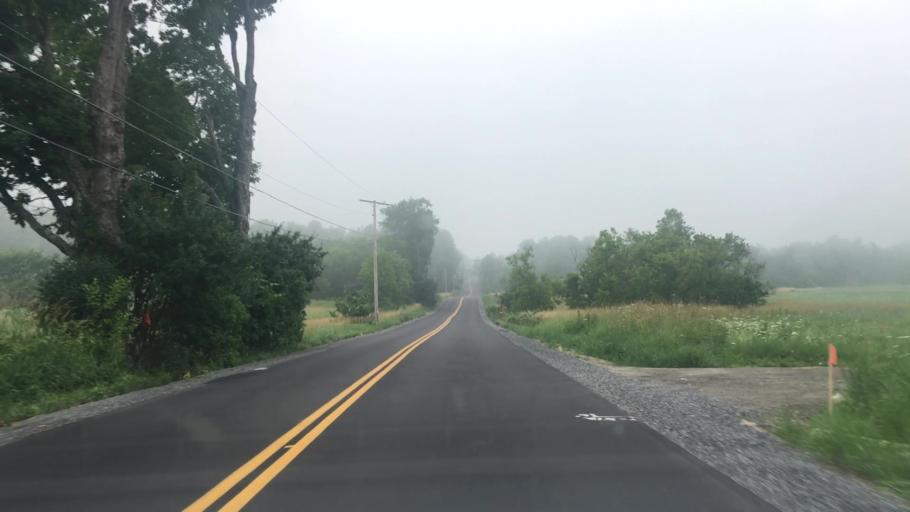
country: US
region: Maine
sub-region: Kennebec County
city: Oakland
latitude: 44.5117
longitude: -69.7098
